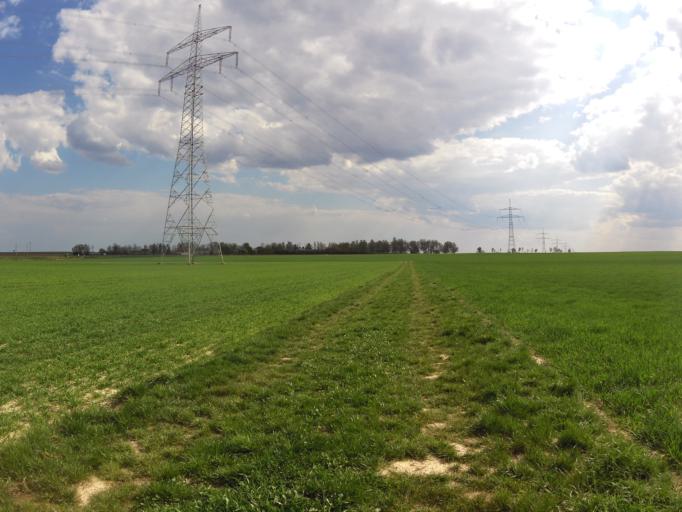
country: DE
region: Bavaria
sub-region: Regierungsbezirk Unterfranken
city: Oberpleichfeld
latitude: 49.8607
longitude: 10.0979
